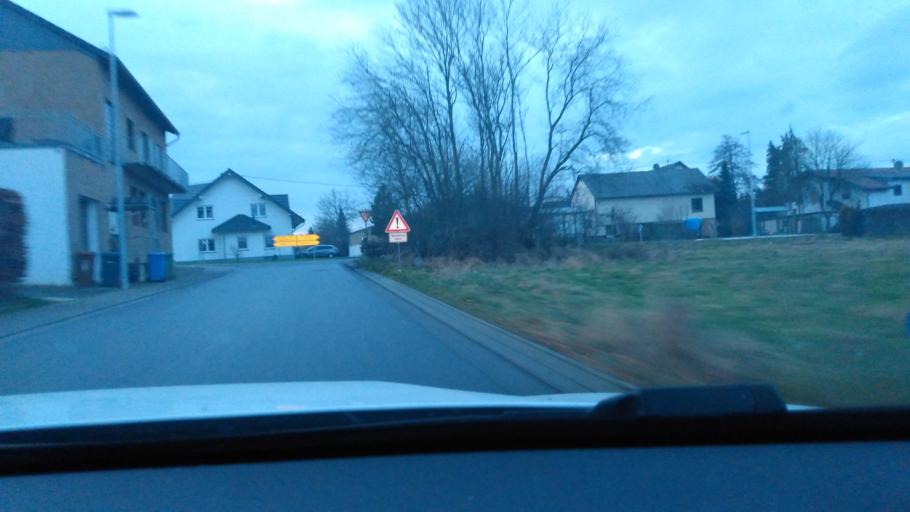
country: DE
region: Rheinland-Pfalz
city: Kircheib
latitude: 50.6886
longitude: 7.4390
